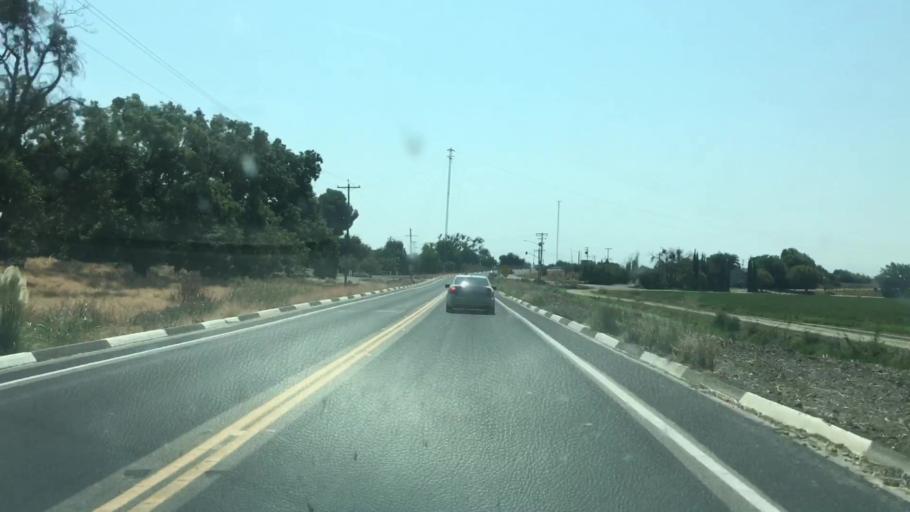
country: US
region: California
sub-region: San Joaquin County
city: Tracy
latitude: 37.8236
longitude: -121.4506
